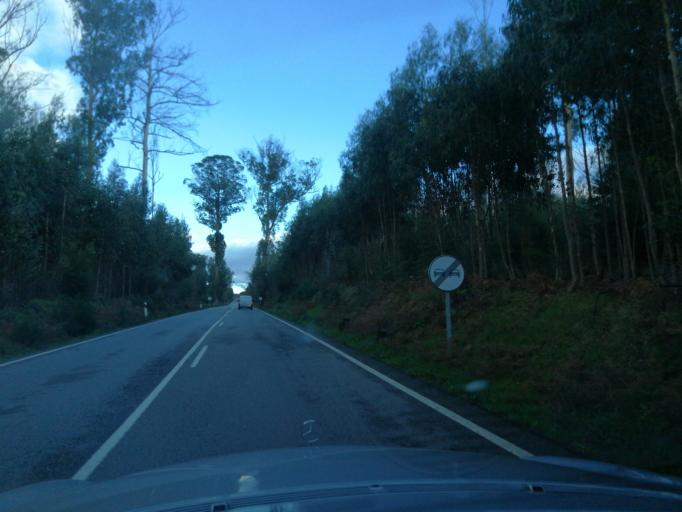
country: PT
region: Braga
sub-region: Esposende
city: Marinhas
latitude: 41.5727
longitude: -8.7087
